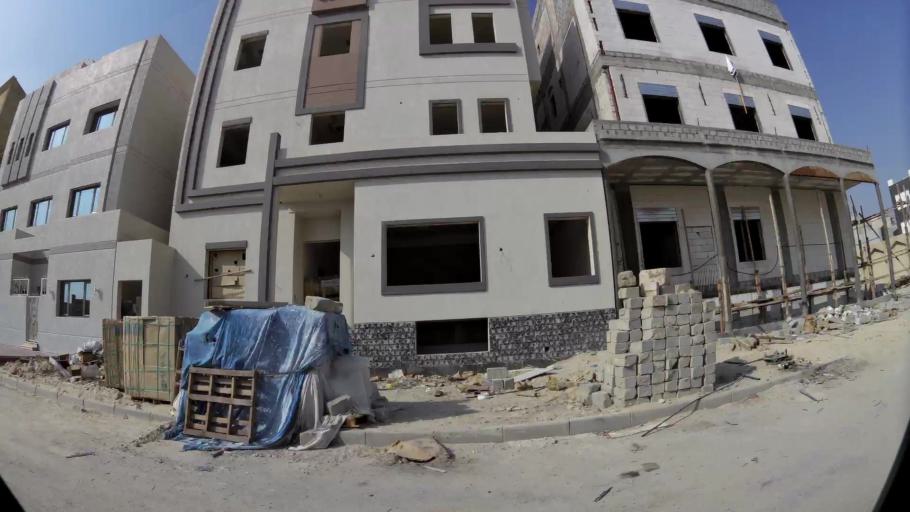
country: KW
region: Muhafazat al Jahra'
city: Al Jahra'
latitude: 29.3478
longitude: 47.7437
